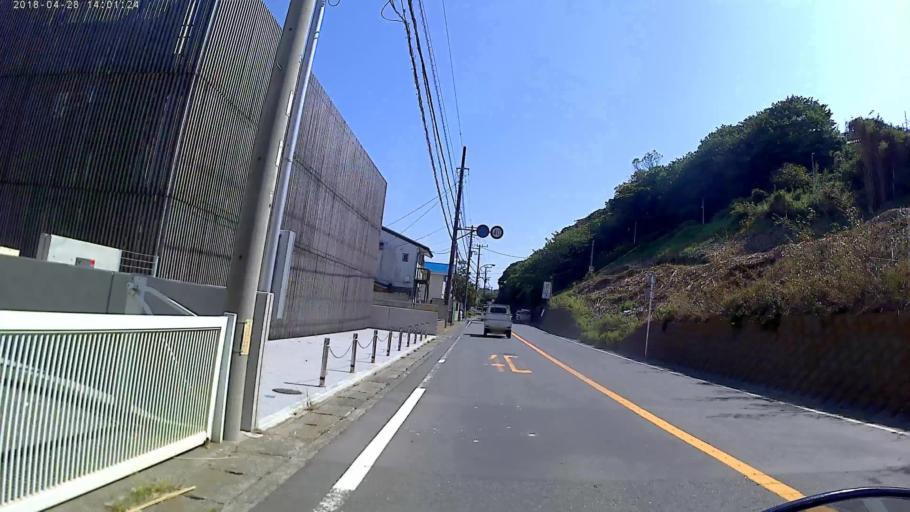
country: JP
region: Kanagawa
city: Miura
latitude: 35.1684
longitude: 139.6593
